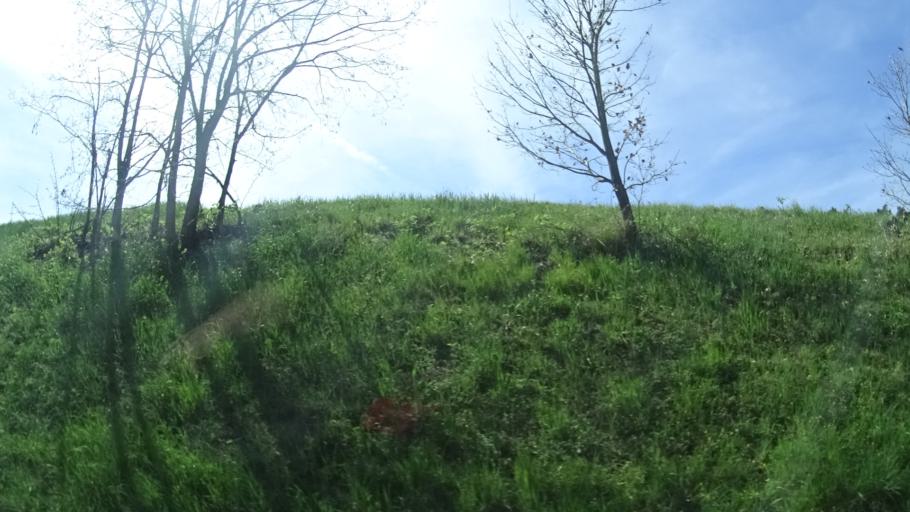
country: DE
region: Bavaria
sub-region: Regierungsbezirk Unterfranken
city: Burgpreppach
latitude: 50.1656
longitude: 10.6349
